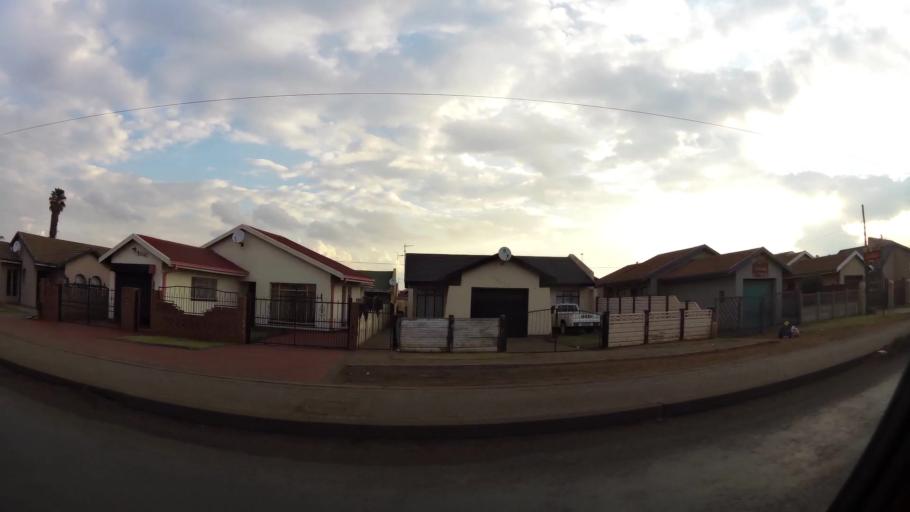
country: ZA
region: Gauteng
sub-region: City of Johannesburg Metropolitan Municipality
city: Orange Farm
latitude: -26.5857
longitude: 27.8450
